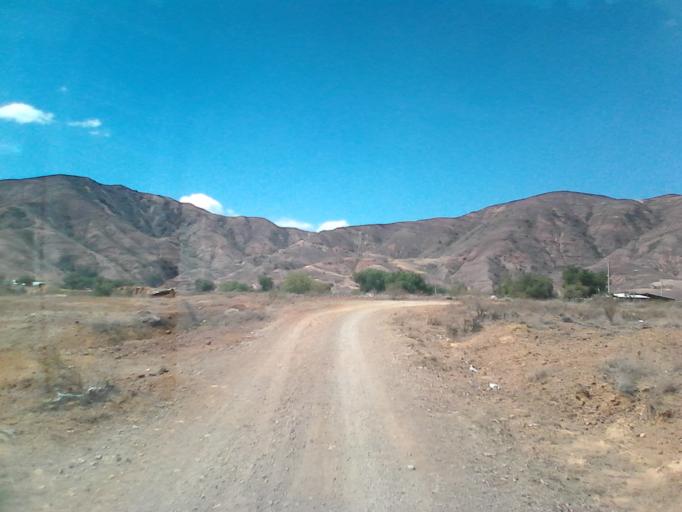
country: CO
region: Boyaca
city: Sachica
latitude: 5.5699
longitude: -73.5434
